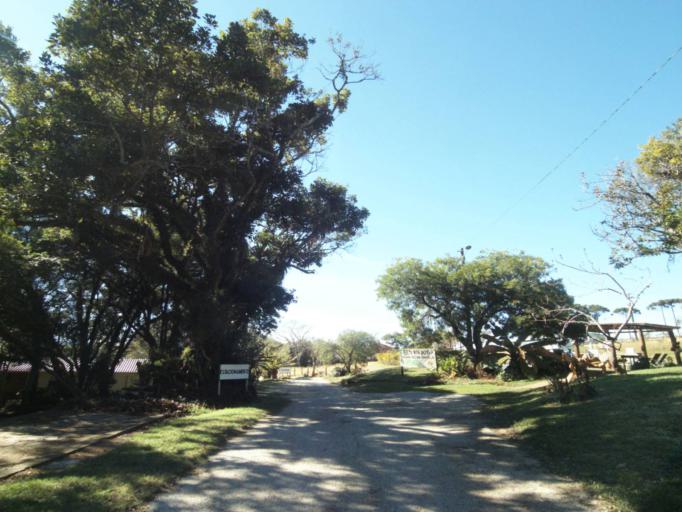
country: BR
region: Parana
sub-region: Tibagi
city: Tibagi
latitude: -24.5248
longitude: -50.3107
